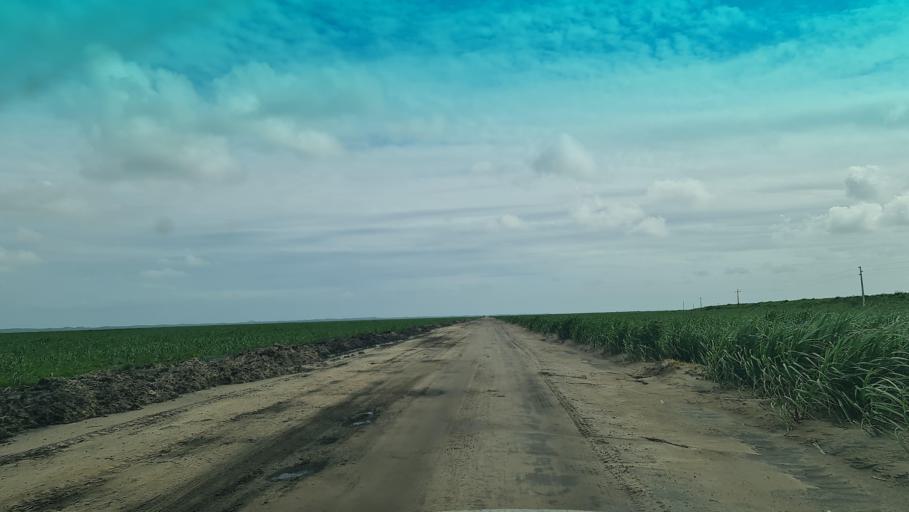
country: MZ
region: Maputo
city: Manhica
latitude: -25.4664
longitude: 32.8177
